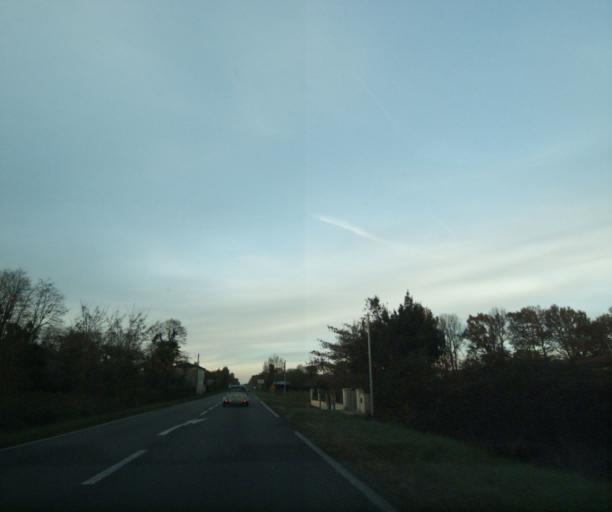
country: FR
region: Aquitaine
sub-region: Departement de la Gironde
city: Bazas
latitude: 44.4878
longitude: -0.2330
